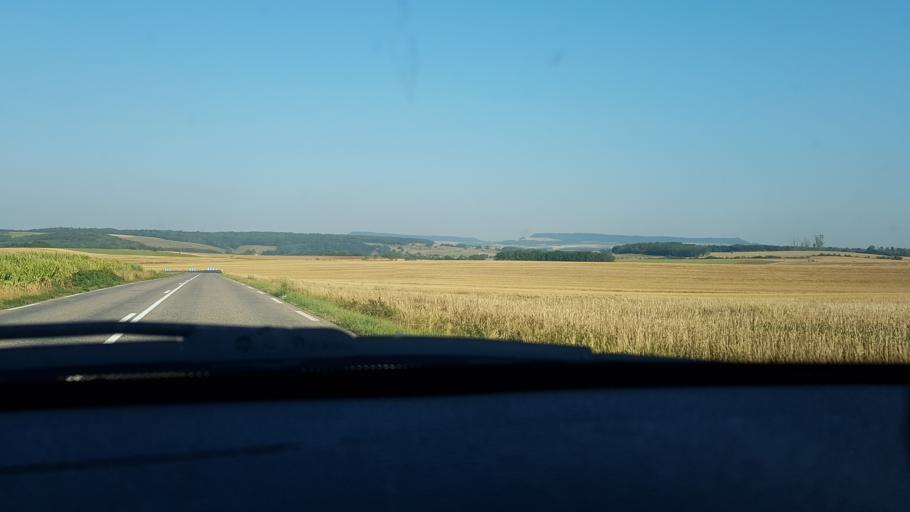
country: FR
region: Lorraine
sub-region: Departement des Vosges
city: Mirecourt
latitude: 48.3581
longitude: 6.1884
